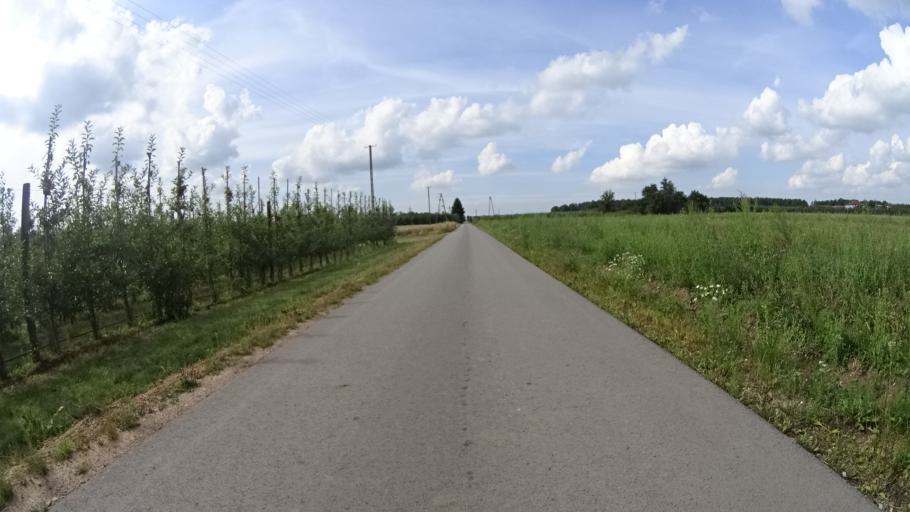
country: PL
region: Masovian Voivodeship
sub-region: Powiat grojecki
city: Goszczyn
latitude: 51.6986
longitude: 20.8187
